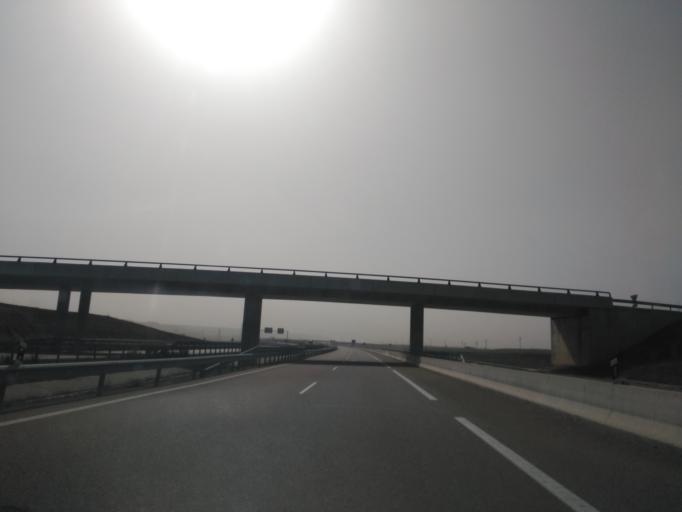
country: ES
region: Castille and Leon
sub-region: Provincia de Palencia
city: Fuentes de Valdepero
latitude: 42.0716
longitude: -4.4923
